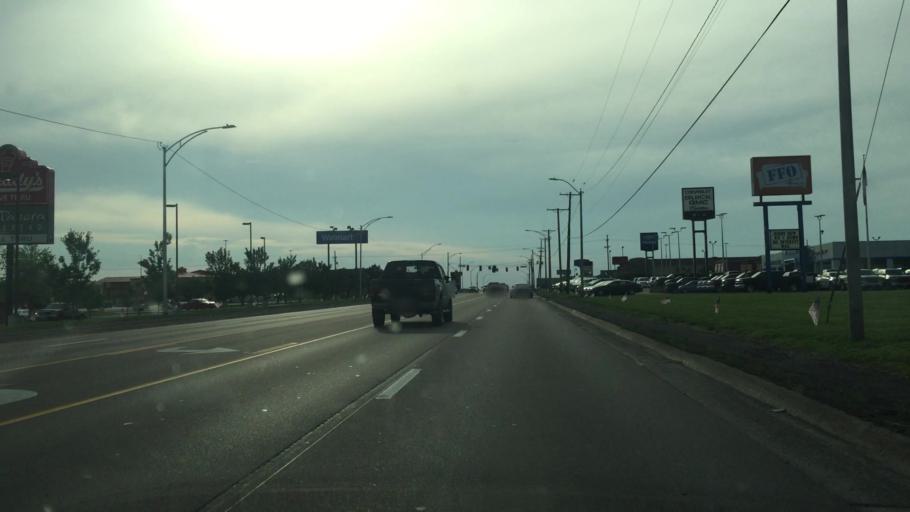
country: US
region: Missouri
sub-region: Pettis County
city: Sedalia
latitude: 38.7094
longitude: -93.2675
